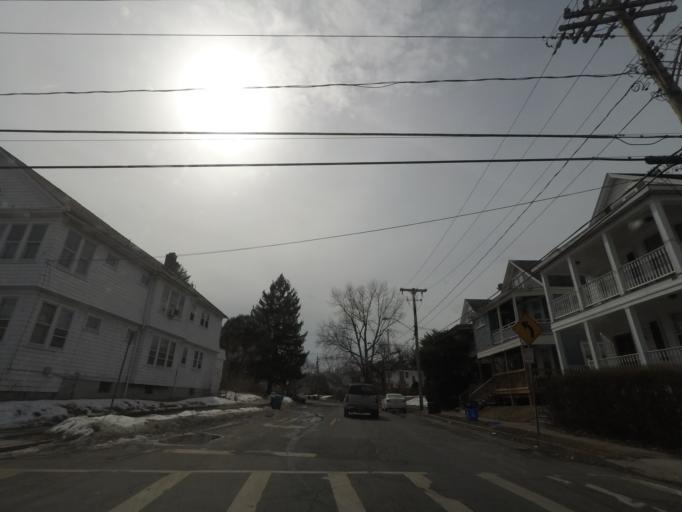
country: US
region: New York
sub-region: Albany County
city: West Albany
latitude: 42.6556
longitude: -73.7875
